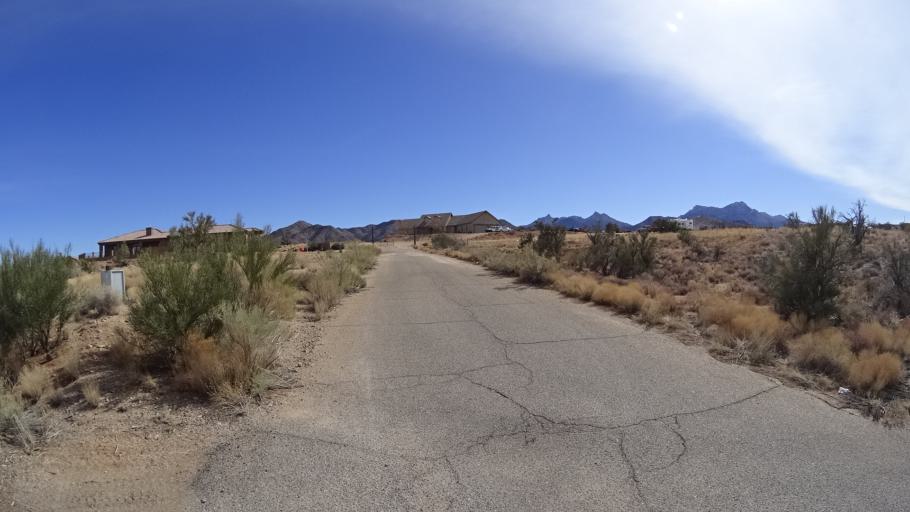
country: US
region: Arizona
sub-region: Mohave County
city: Kingman
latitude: 35.1714
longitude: -113.9780
